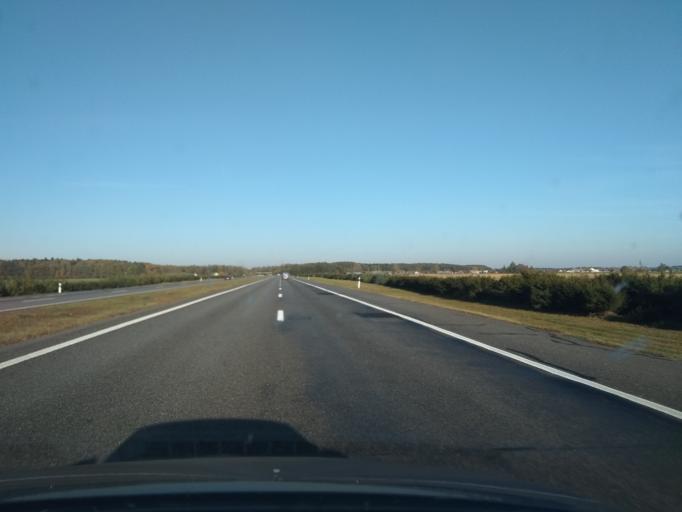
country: BY
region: Brest
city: Ivatsevichy
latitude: 52.6708
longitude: 25.3061
